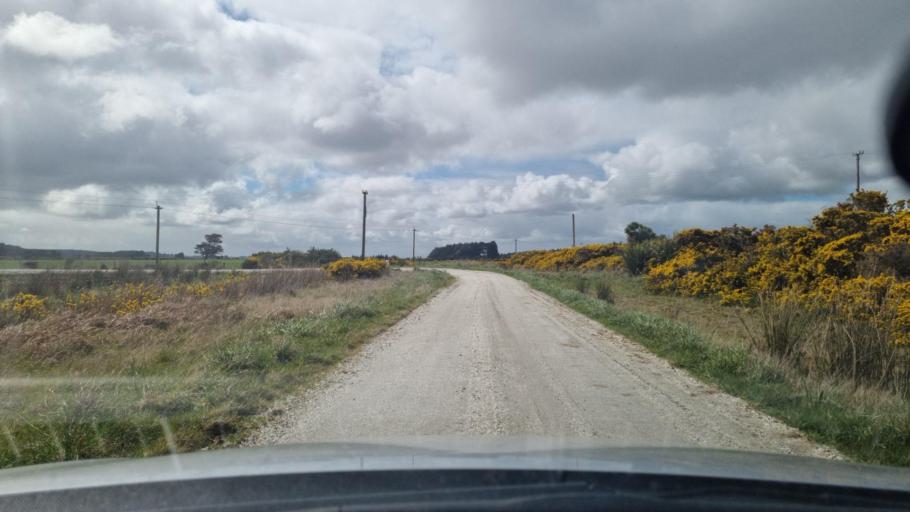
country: NZ
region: Southland
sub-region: Invercargill City
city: Bluff
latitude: -46.5266
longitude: 168.3075
